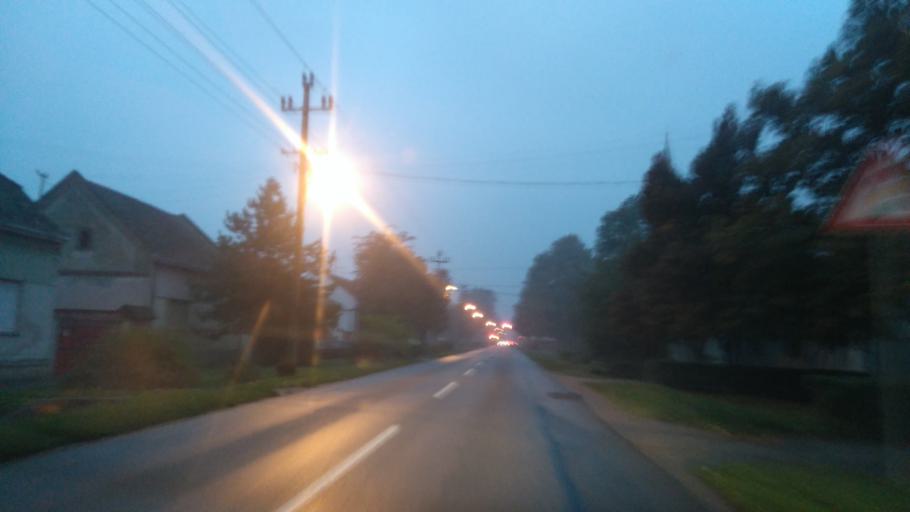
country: RS
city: Mol
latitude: 45.7617
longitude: 20.1299
